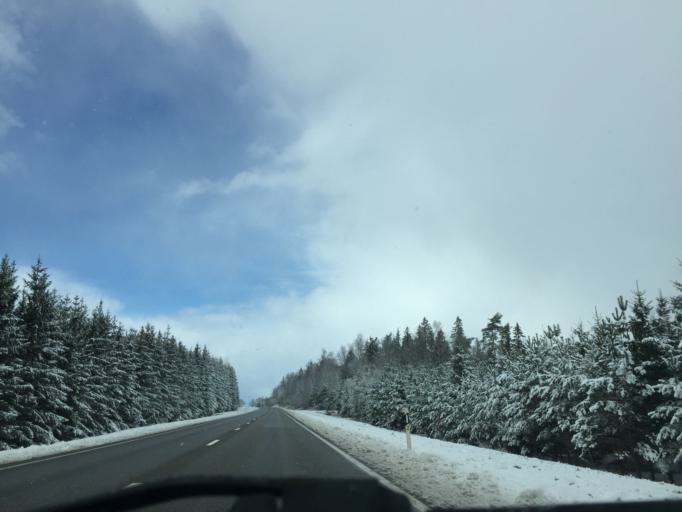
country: LV
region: Talsu Rajons
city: Talsi
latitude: 57.1779
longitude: 22.6438
